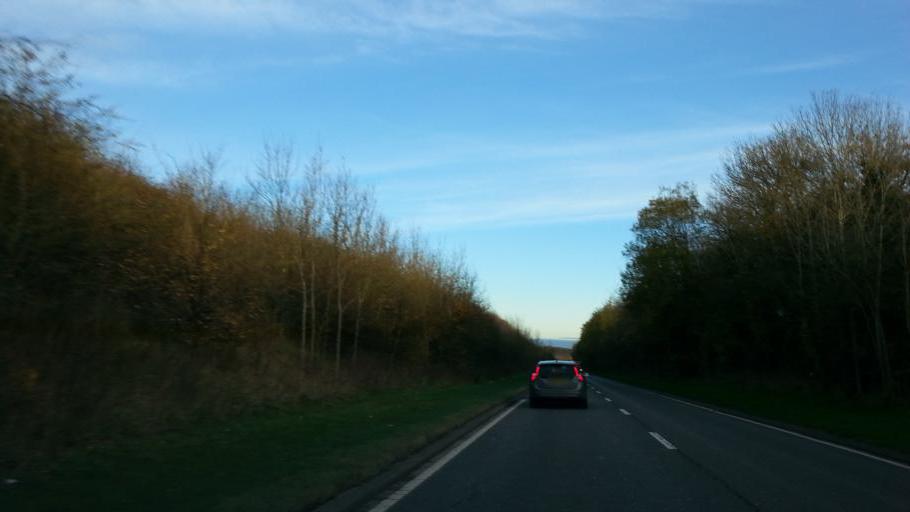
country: GB
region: England
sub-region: Northamptonshire
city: Corby
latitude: 52.4993
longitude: -0.6420
